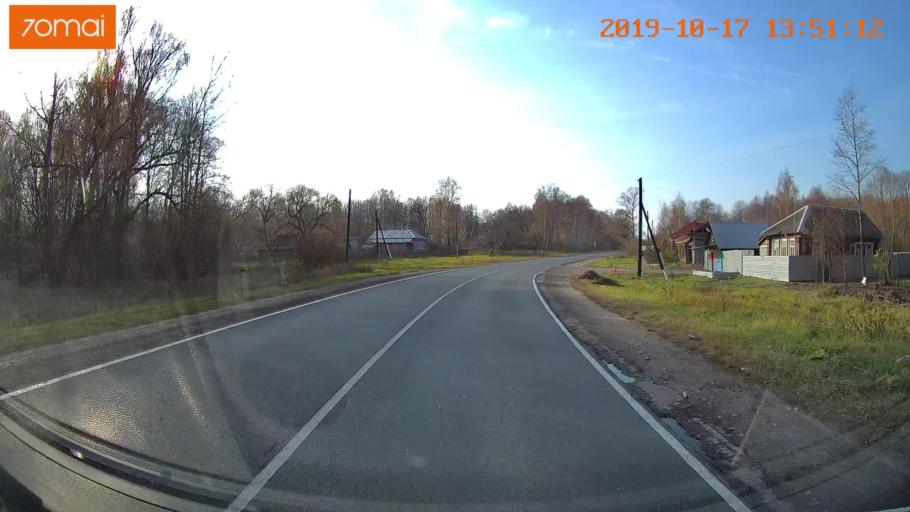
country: RU
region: Rjazan
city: Tuma
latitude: 55.1396
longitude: 40.3929
